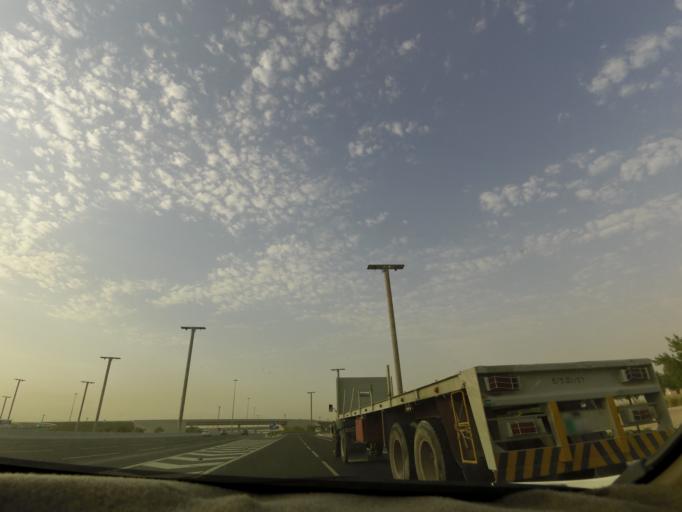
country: QA
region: Al Wakrah
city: Al Wakrah
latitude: 25.2443
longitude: 51.5893
